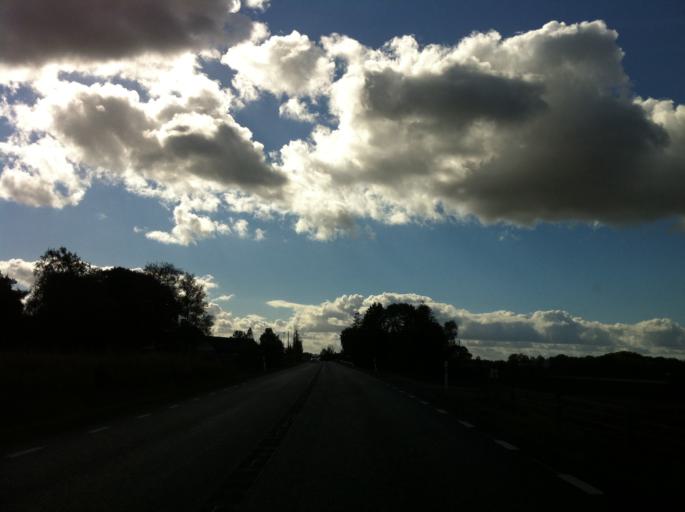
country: SE
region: Skane
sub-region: Tomelilla Kommun
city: Tomelilla
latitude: 55.6476
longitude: 14.0143
